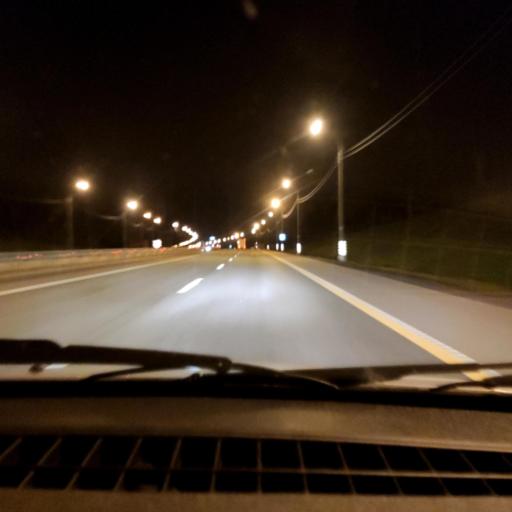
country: RU
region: Lipetsk
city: Khlevnoye
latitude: 52.2979
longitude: 39.0519
